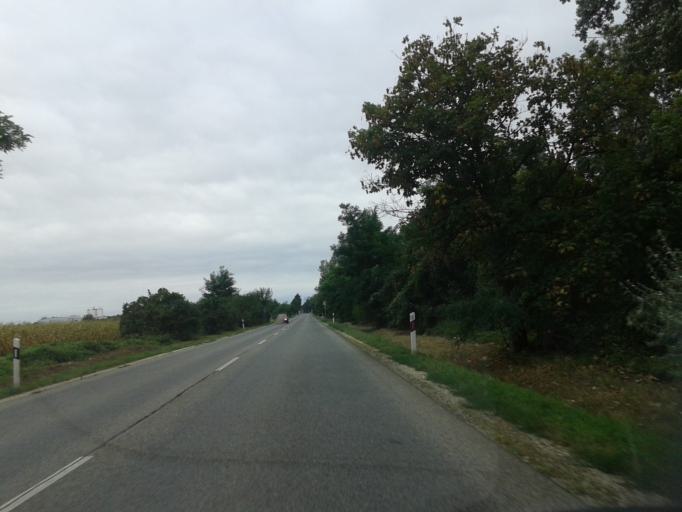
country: HU
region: Pest
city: Dunavarsany
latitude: 47.2668
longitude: 19.0298
